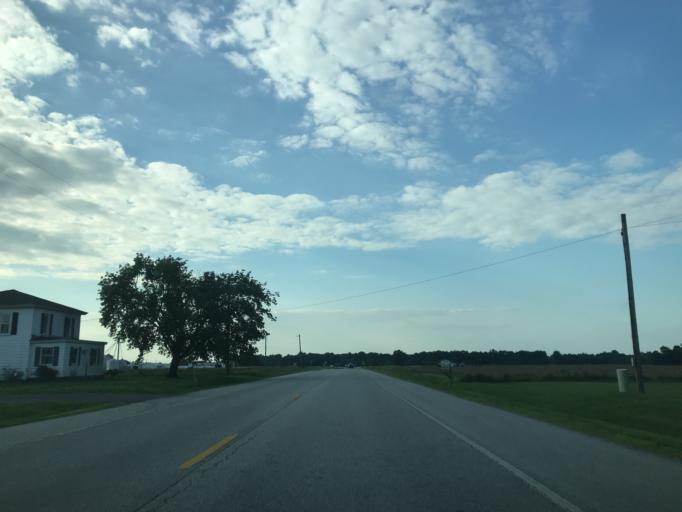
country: US
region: Maryland
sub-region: Caroline County
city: Federalsburg
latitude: 38.7422
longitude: -75.7933
